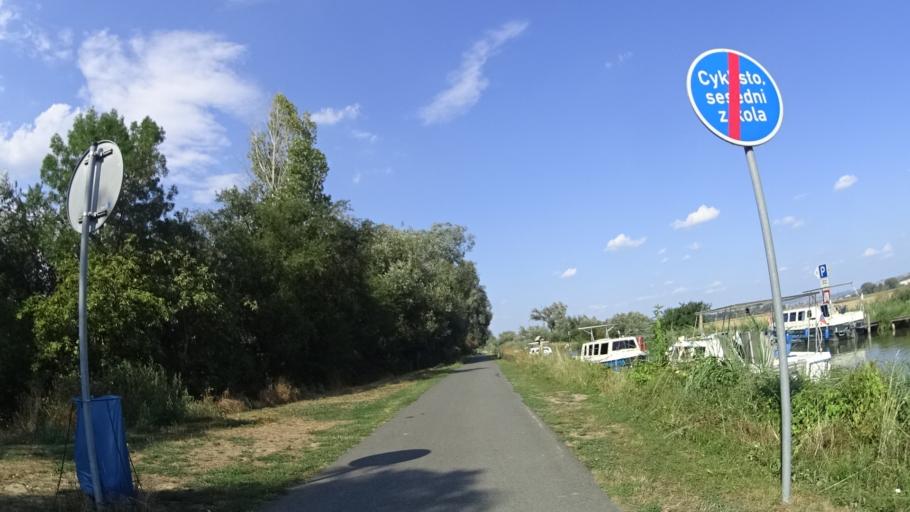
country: CZ
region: Zlin
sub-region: Okres Uherske Hradiste
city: Uherske Hradiste
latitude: 49.0850
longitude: 17.4672
